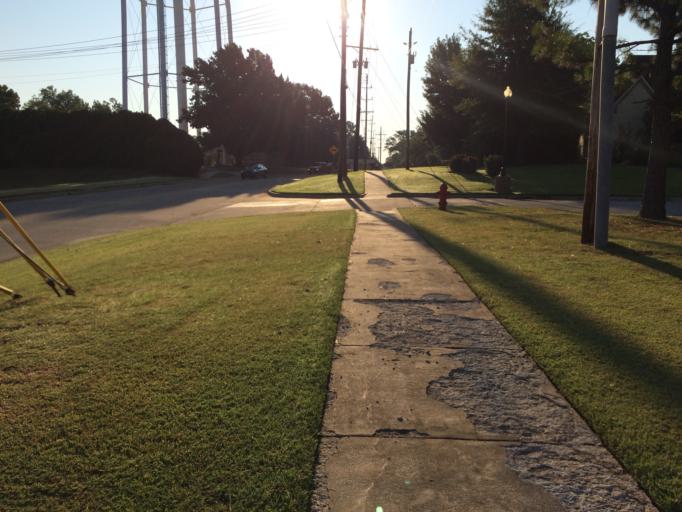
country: US
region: Oklahoma
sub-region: Cleveland County
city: Norman
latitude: 35.2112
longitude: -97.4755
